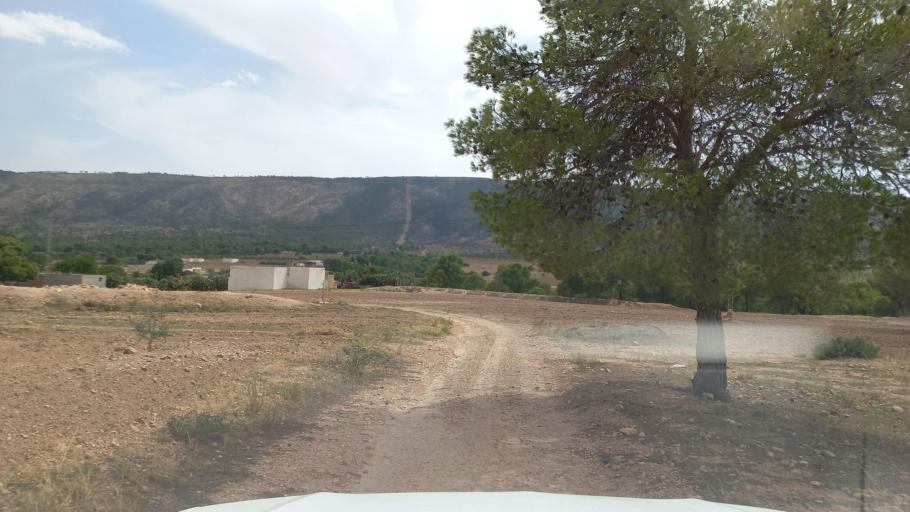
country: TN
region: Al Qasrayn
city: Kasserine
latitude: 35.3689
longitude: 8.8938
